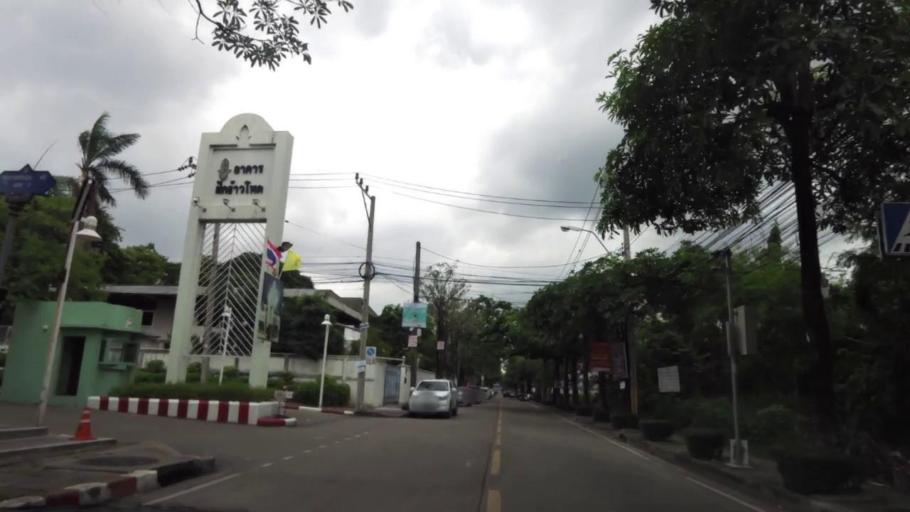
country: TH
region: Bangkok
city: Bang Kapi
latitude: 13.7580
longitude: 100.6393
